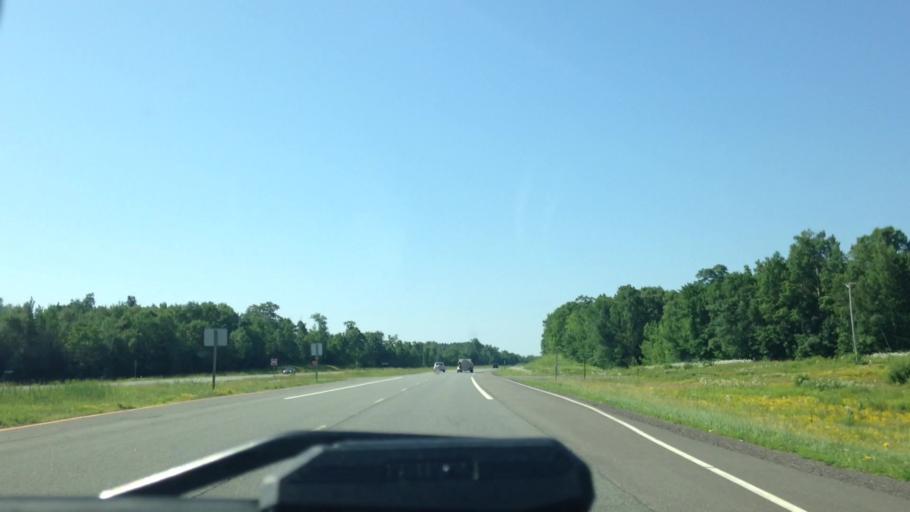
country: US
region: Wisconsin
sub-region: Douglas County
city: Lake Nebagamon
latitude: 46.4182
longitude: -91.8099
